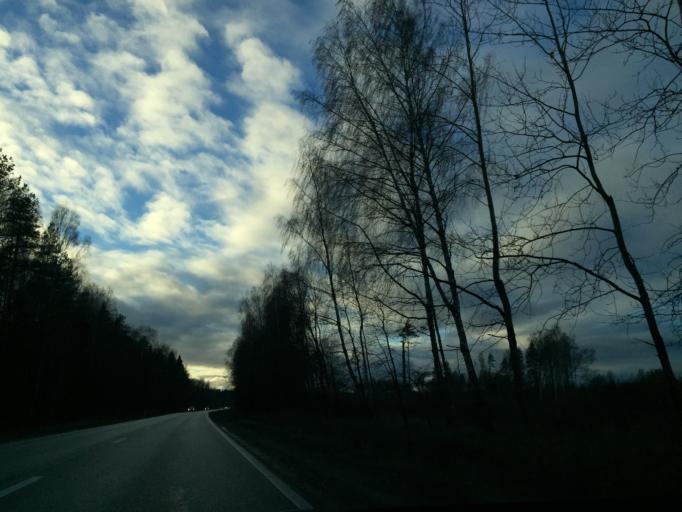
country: LV
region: Pargaujas
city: Stalbe
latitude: 57.3692
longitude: 25.0028
